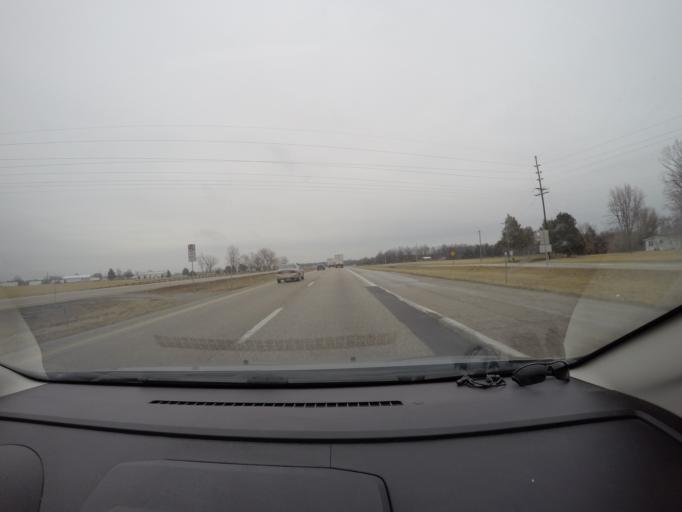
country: US
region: Missouri
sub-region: Montgomery County
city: Montgomery City
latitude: 38.8718
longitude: -91.3684
